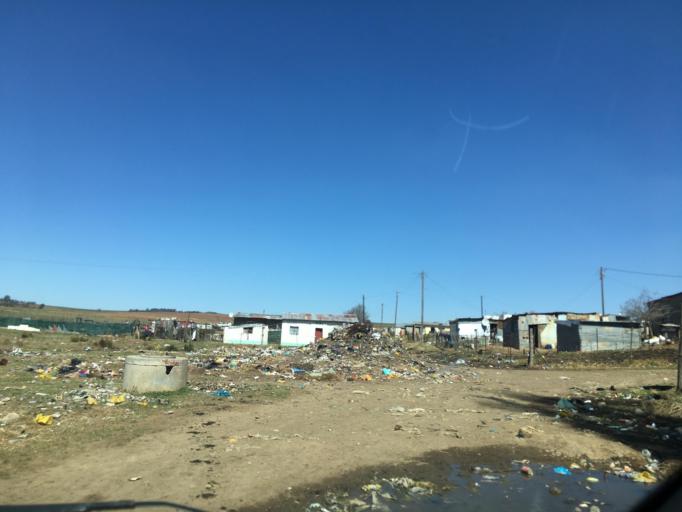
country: ZA
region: Eastern Cape
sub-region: Chris Hani District Municipality
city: Elliot
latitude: -31.3318
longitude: 27.8261
